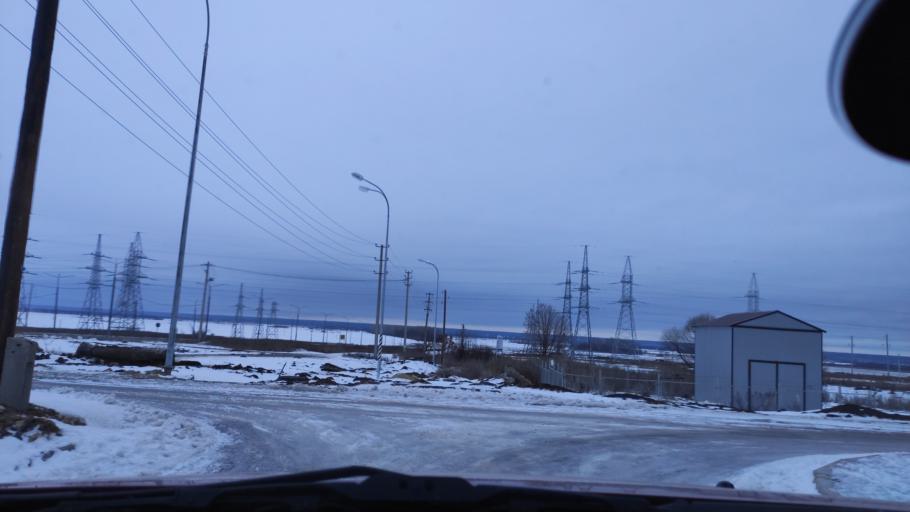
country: RU
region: Tambov
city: Tambov
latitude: 52.7845
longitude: 41.4205
